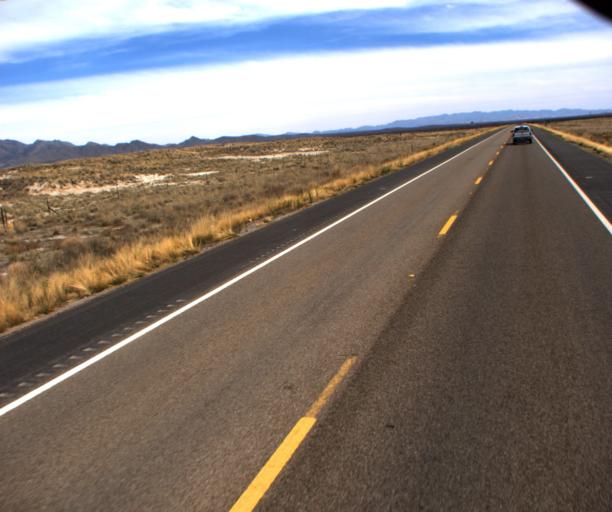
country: US
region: Arizona
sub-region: Cochise County
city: Willcox
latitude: 32.2069
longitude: -109.7736
